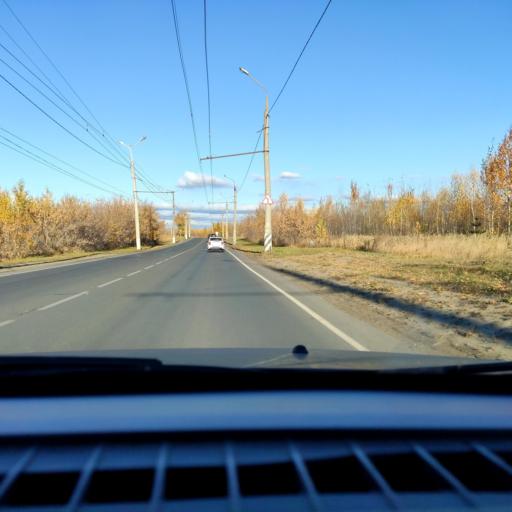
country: RU
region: Samara
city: Tol'yatti
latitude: 53.4811
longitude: 49.3756
